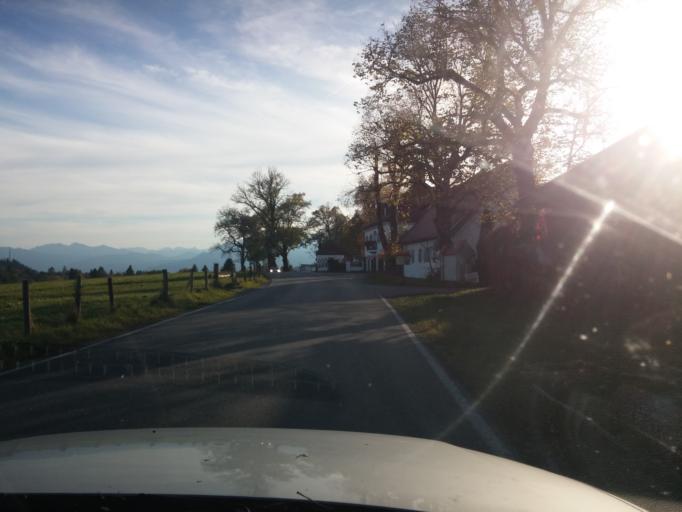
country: DE
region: Bavaria
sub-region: Upper Bavaria
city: Bad Toelz
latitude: 47.7680
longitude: 11.5709
